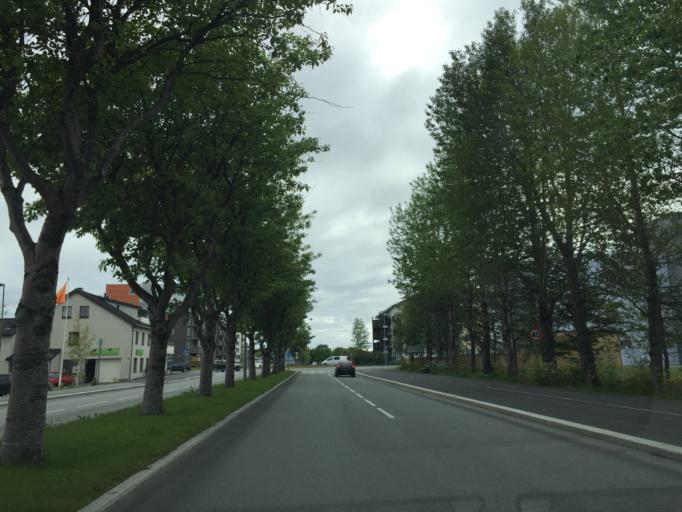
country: NO
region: Nordland
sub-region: Bodo
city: Bodo
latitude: 67.2800
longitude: 14.4181
